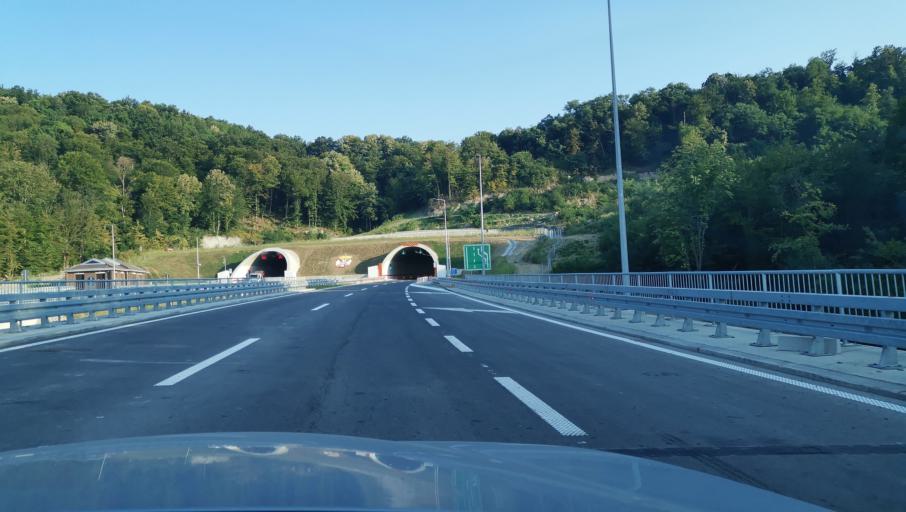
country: RS
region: Central Serbia
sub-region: Kolubarski Okrug
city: Ljig
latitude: 44.2125
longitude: 20.2621
